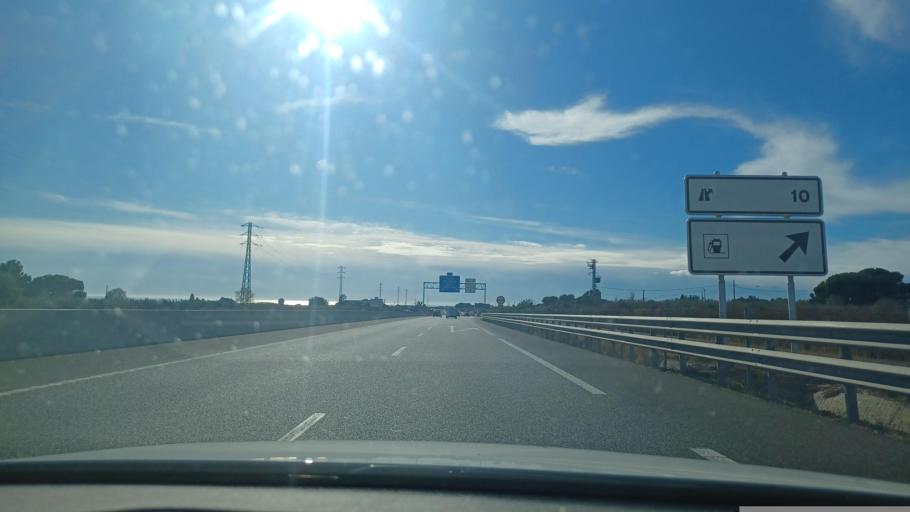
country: ES
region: Catalonia
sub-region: Provincia de Tarragona
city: La Selva
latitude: 41.1885
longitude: 1.1374
